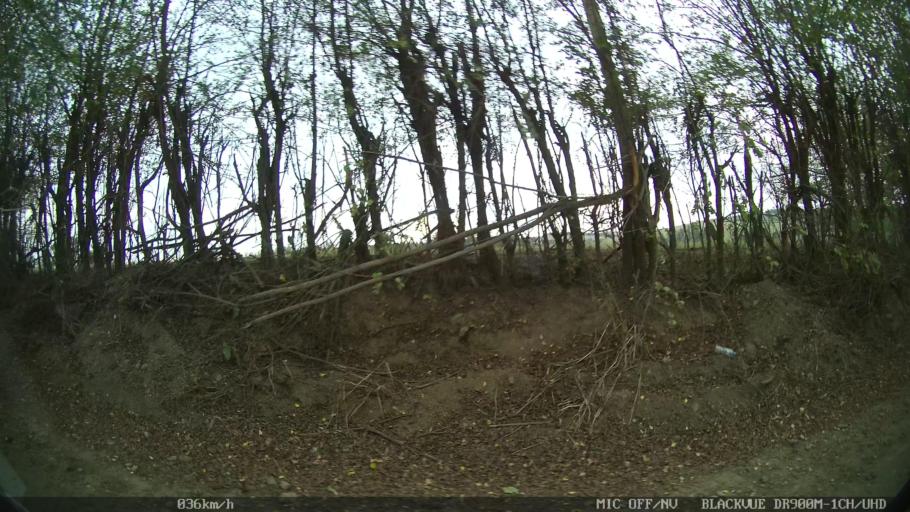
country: BR
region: Sao Paulo
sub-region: Americana
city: Americana
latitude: -22.6608
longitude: -47.3720
